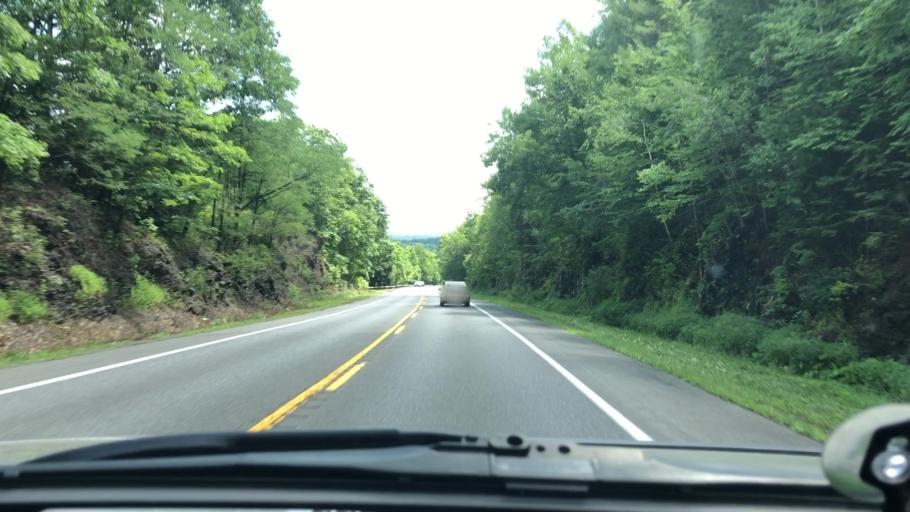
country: US
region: New York
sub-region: Ulster County
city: Saugerties
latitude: 42.1182
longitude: -73.9852
